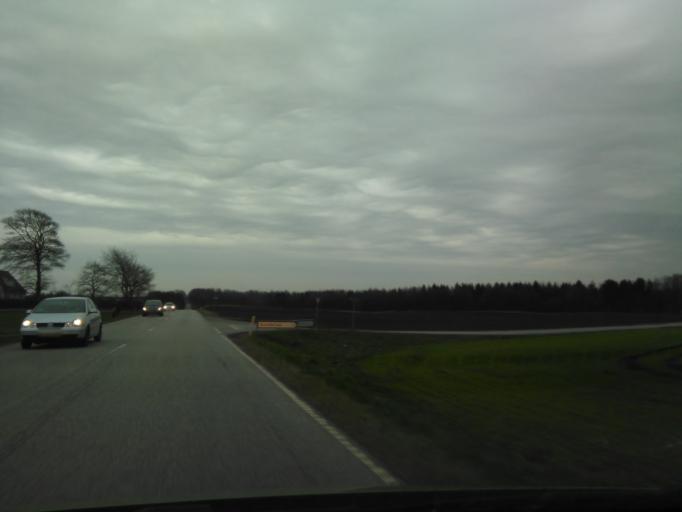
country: DK
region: North Denmark
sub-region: Mariagerfjord Kommune
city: Mariager
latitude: 56.6151
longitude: 9.9861
